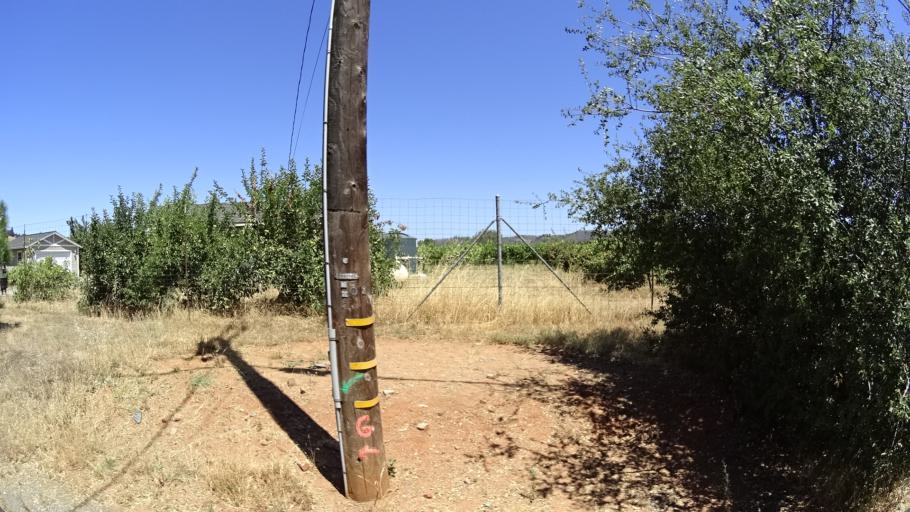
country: US
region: California
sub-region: Calaveras County
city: Mountain Ranch
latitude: 38.2159
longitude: -120.5419
